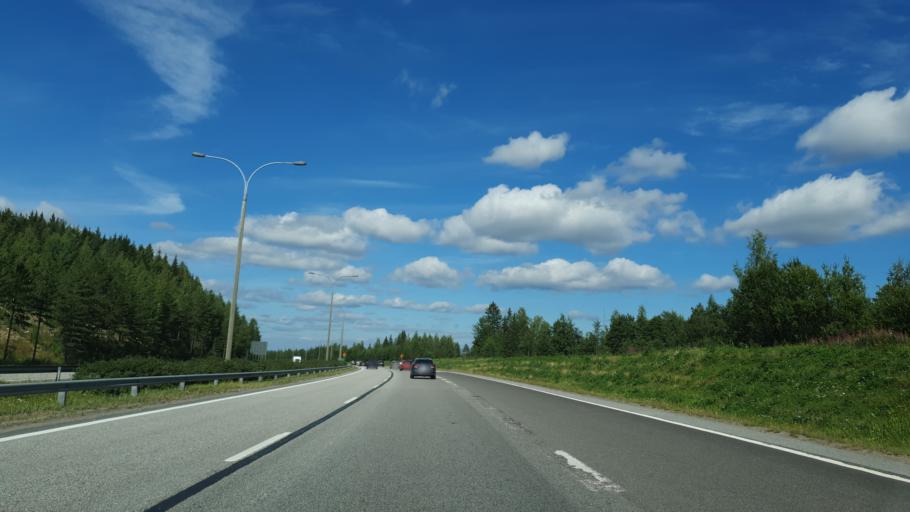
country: FI
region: Central Finland
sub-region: Jyvaeskylae
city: Jyvaeskylae
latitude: 62.1937
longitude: 25.7052
